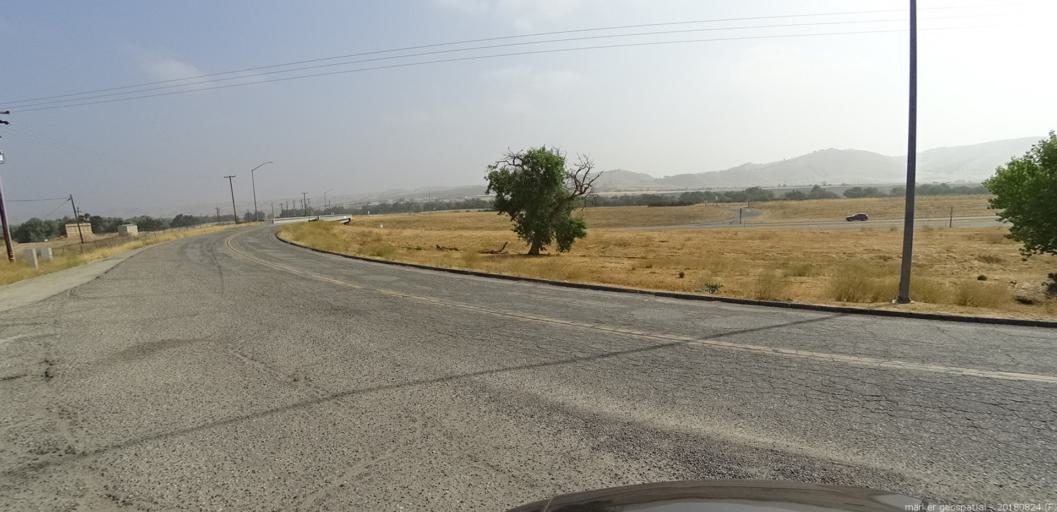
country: US
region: California
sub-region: San Luis Obispo County
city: San Miguel
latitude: 35.8141
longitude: -120.7554
